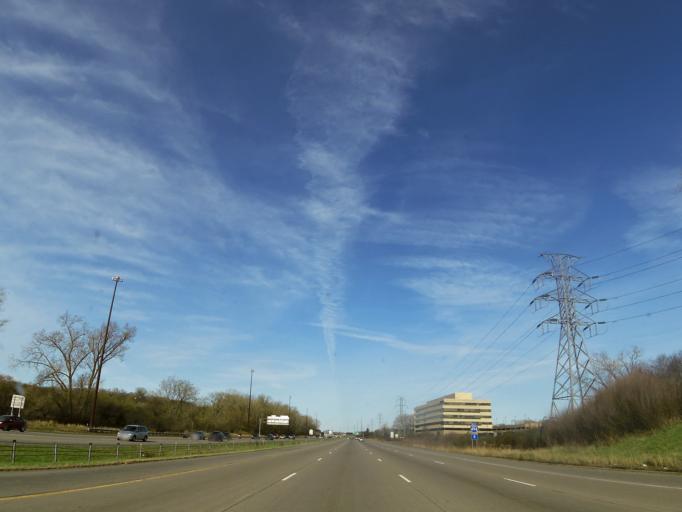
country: US
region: Minnesota
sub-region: Hennepin County
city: Edina
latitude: 44.8598
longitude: -93.3629
